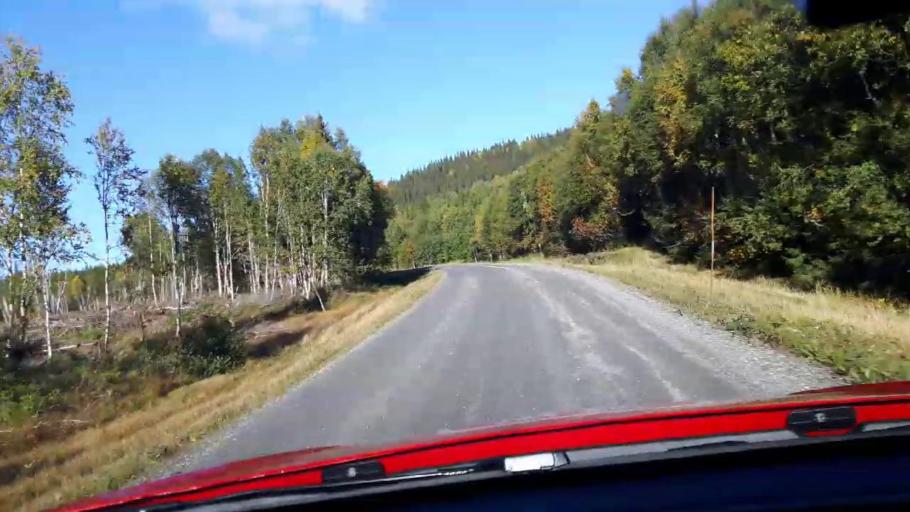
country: NO
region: Nord-Trondelag
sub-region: Lierne
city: Sandvika
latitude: 64.5903
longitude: 13.8564
